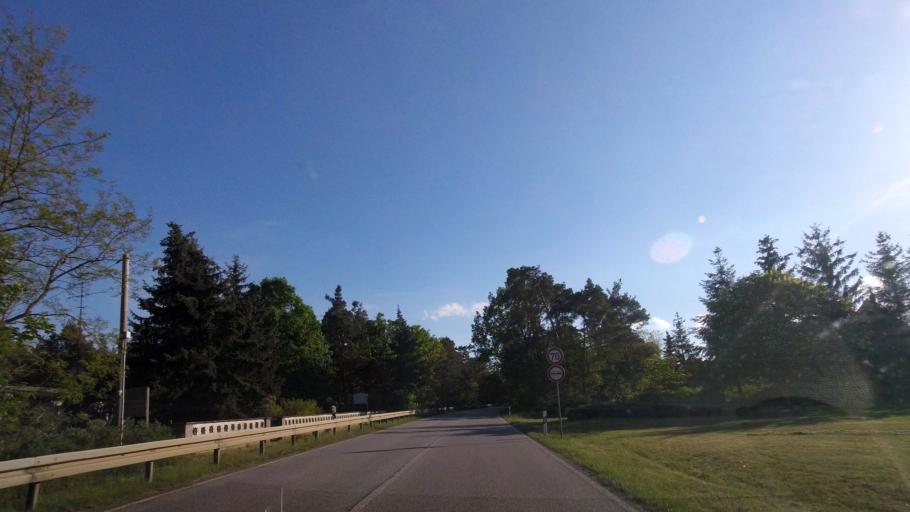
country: DE
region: Brandenburg
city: Luebben
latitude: 51.9095
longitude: 13.8627
